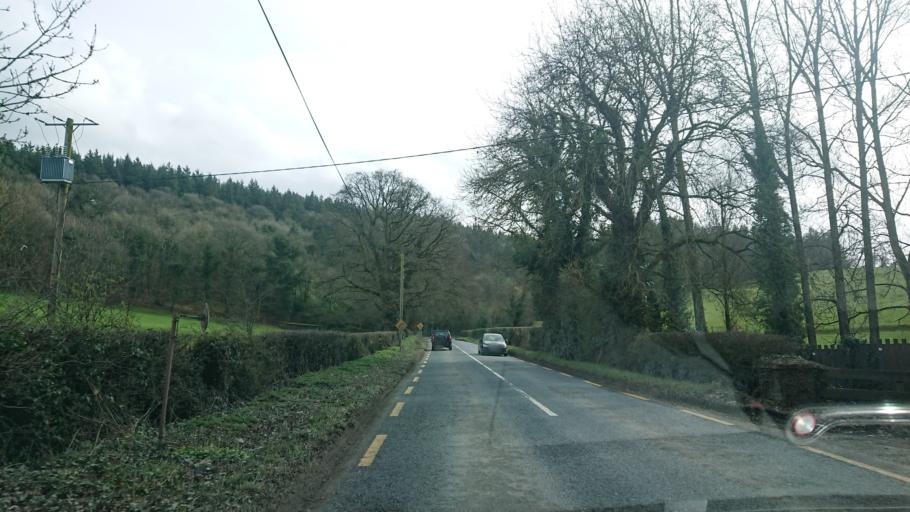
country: IE
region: Leinster
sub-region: Kildare
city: Eadestown
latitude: 53.1862
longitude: -6.5580
